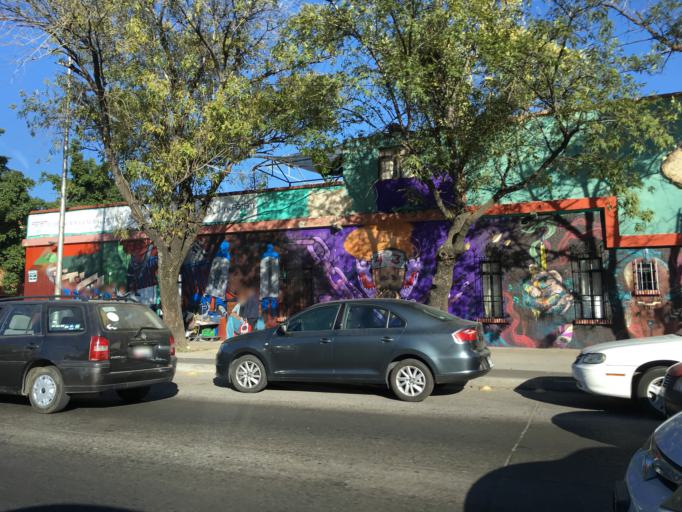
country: MX
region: Jalisco
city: Guadalajara
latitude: 20.6836
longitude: -103.3539
